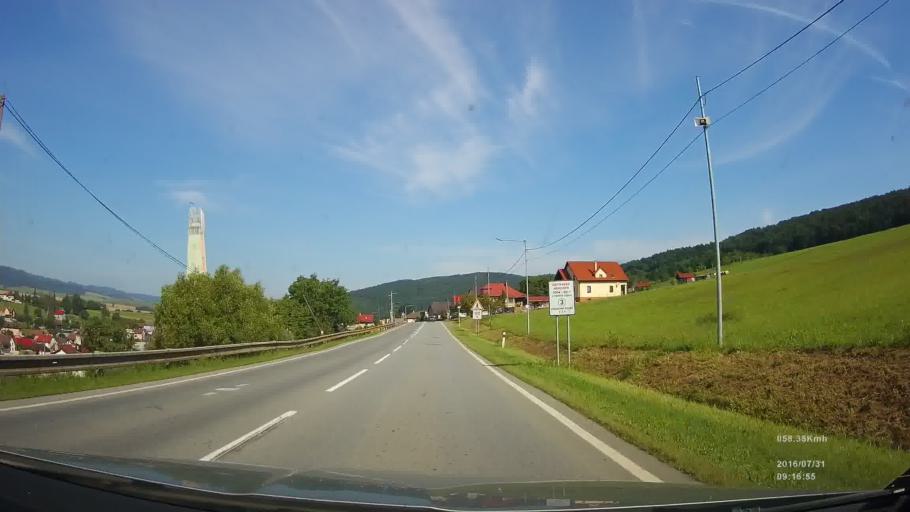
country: SK
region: Presovsky
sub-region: Okres Bardejov
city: Bardejov
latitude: 49.2453
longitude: 21.2627
